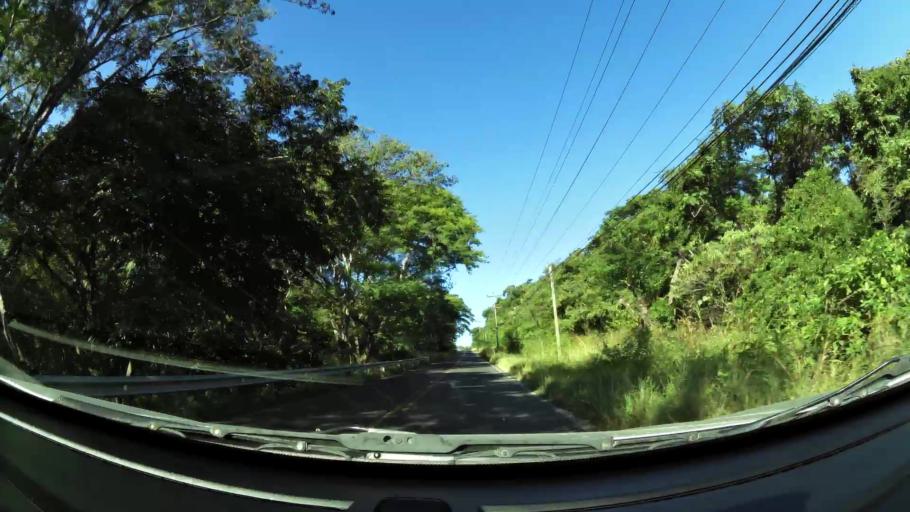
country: CR
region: Guanacaste
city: Belen
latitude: 10.3634
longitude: -85.6614
